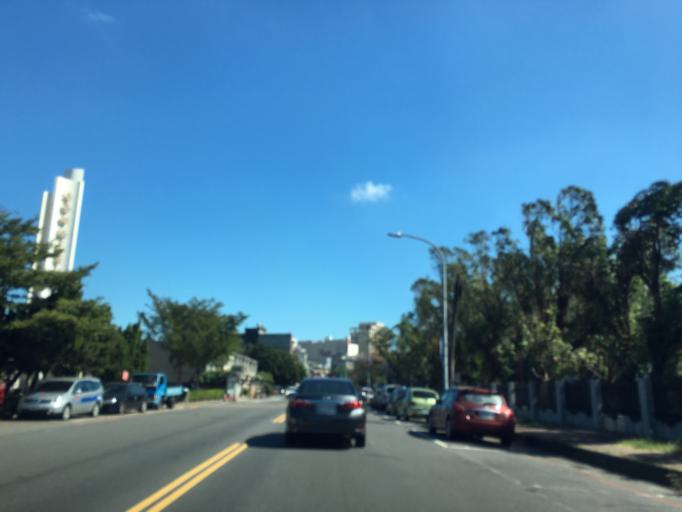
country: TW
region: Taiwan
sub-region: Hsinchu
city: Hsinchu
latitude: 24.8040
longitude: 120.9582
